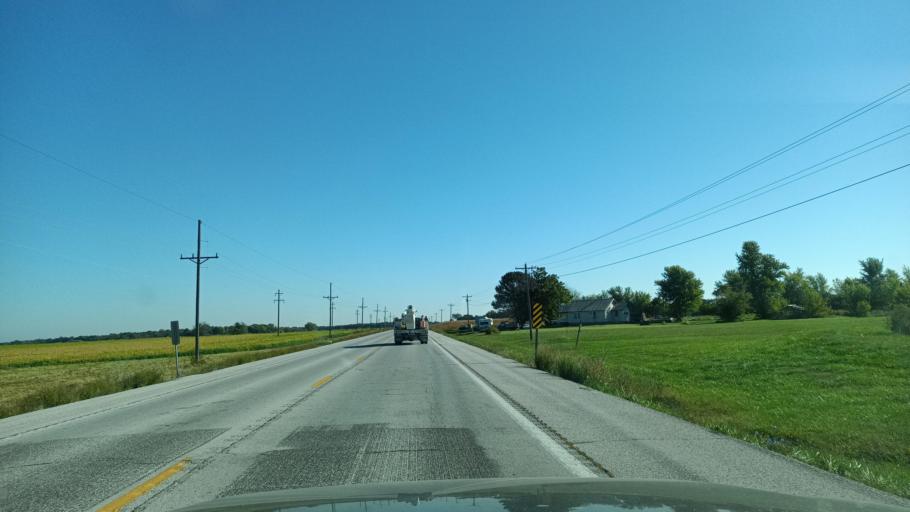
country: US
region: Missouri
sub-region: Audrain County
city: Vandalia
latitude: 39.4490
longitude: -91.6289
